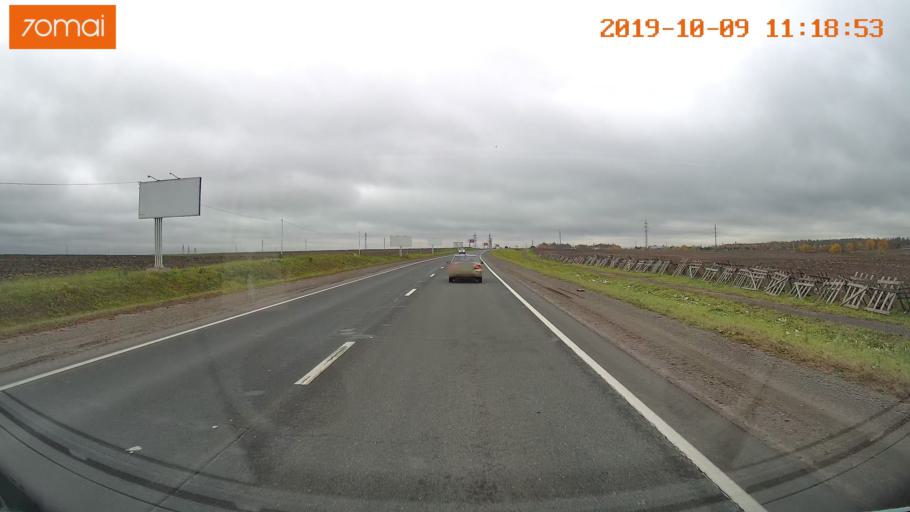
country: RU
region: Vologda
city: Vologda
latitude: 59.1641
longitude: 39.9212
